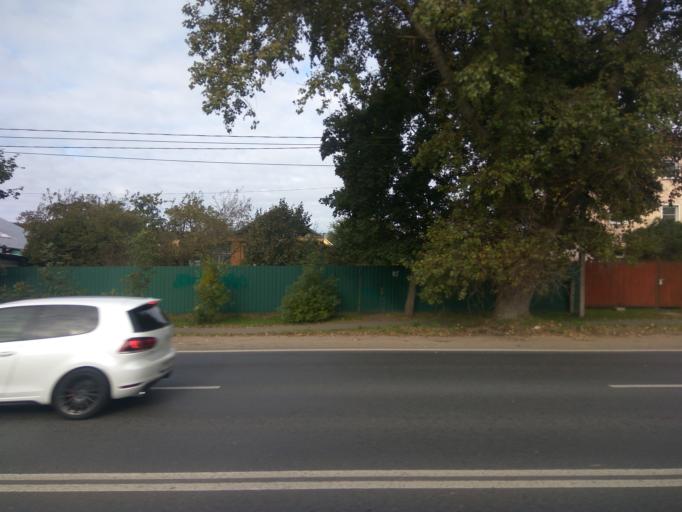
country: RU
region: Moskovskaya
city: Medvezh'i Ozera
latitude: 55.8605
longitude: 37.9853
